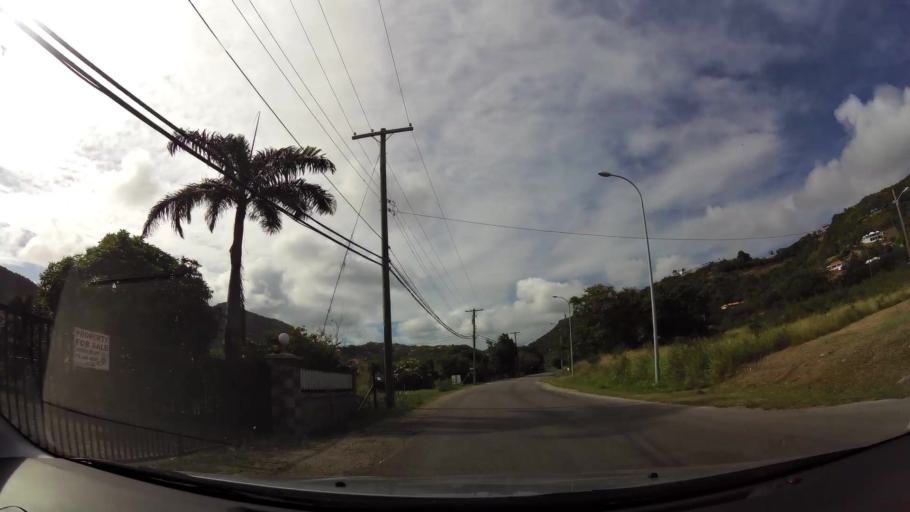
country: AG
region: Saint Paul
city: Falmouth
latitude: 17.0253
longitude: -61.7797
